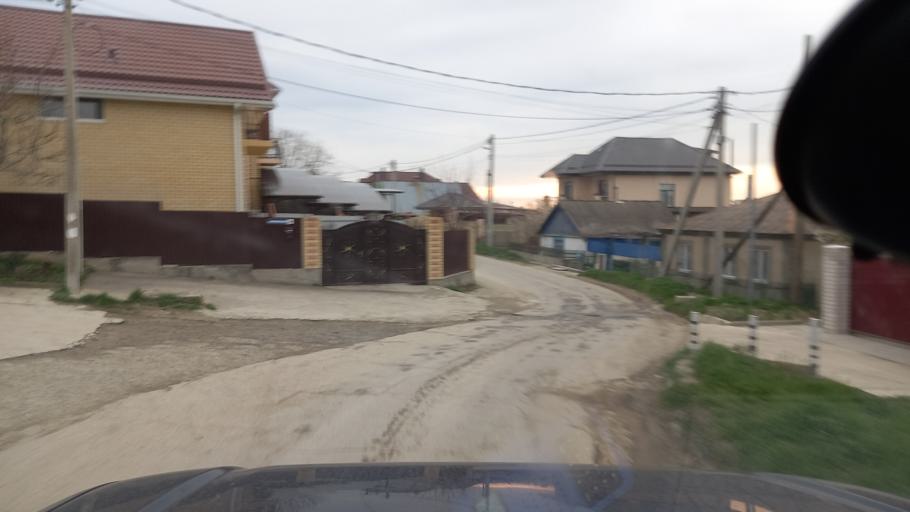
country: RU
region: Krasnodarskiy
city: Anapa
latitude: 44.8505
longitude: 37.3516
